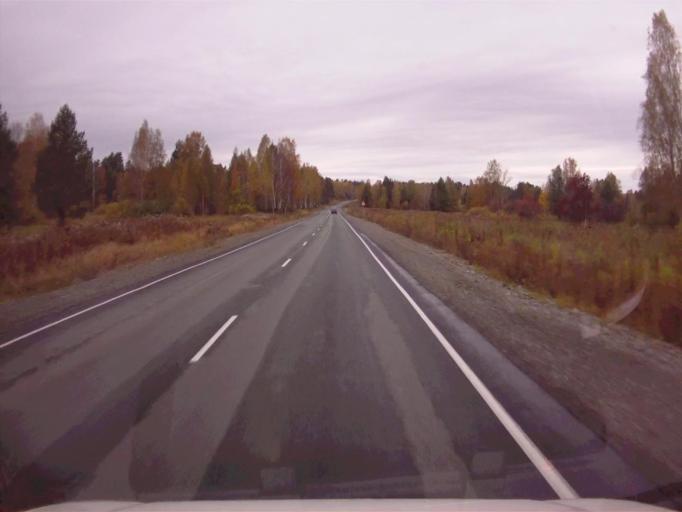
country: RU
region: Chelyabinsk
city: Nyazepetrovsk
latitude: 56.0448
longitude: 59.7632
